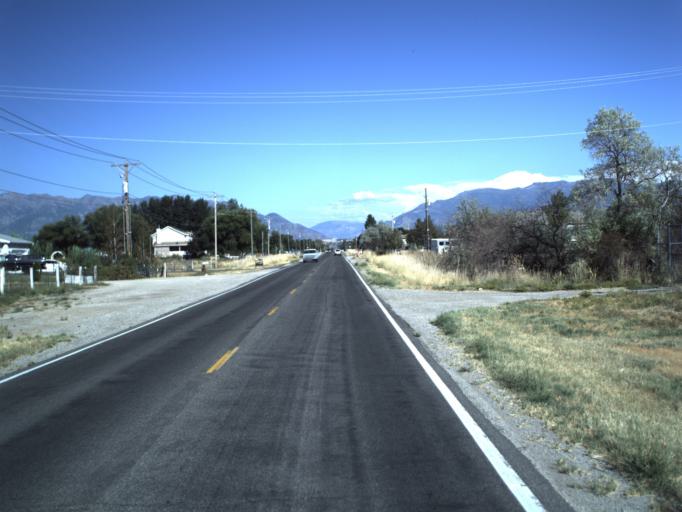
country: US
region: Utah
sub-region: Weber County
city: Hooper
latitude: 41.1399
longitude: -112.1056
